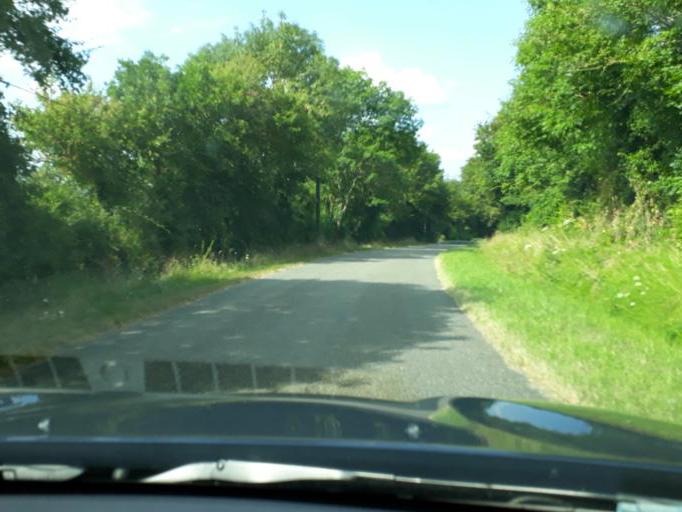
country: FR
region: Centre
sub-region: Departement du Cher
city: Jouet-sur-l'Aubois
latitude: 47.0016
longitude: 2.9119
